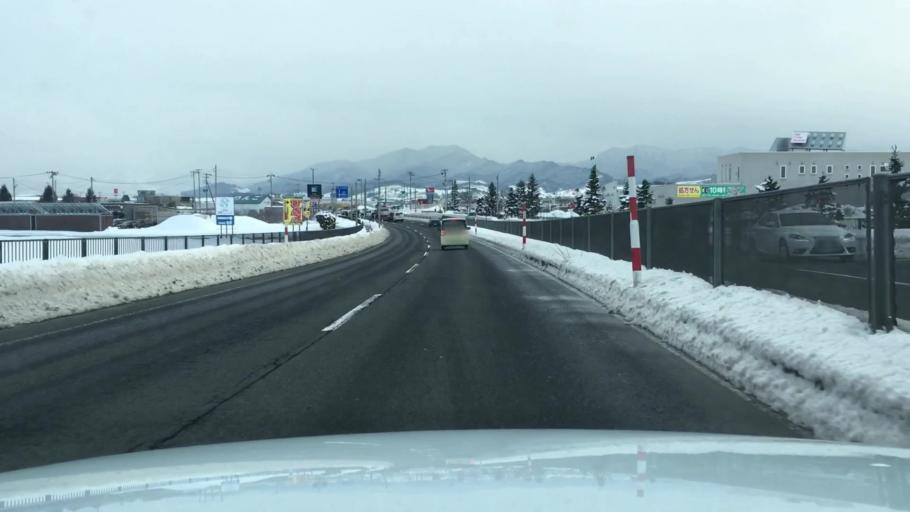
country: JP
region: Aomori
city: Hirosaki
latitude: 40.5877
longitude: 140.5069
